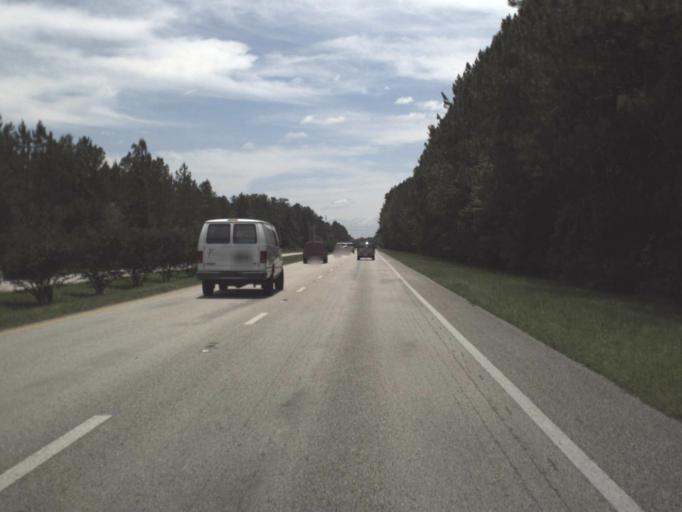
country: US
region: Florida
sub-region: Nassau County
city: Nassau Village-Ratliff
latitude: 30.4626
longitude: -81.7753
